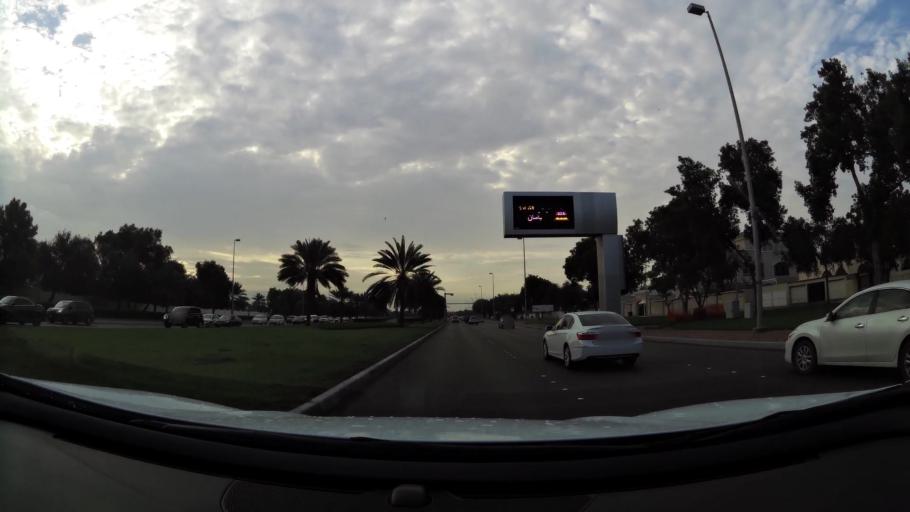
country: AE
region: Abu Dhabi
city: Abu Dhabi
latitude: 24.4380
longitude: 54.3731
